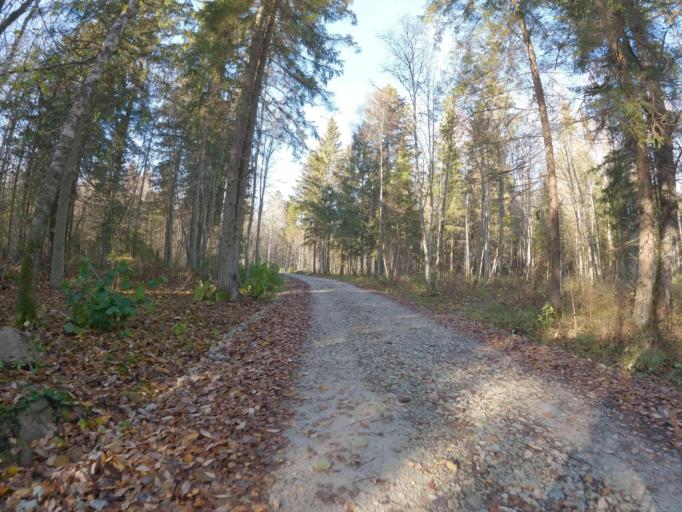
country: EE
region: Raplamaa
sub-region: Rapla vald
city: Rapla
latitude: 59.0082
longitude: 24.8099
